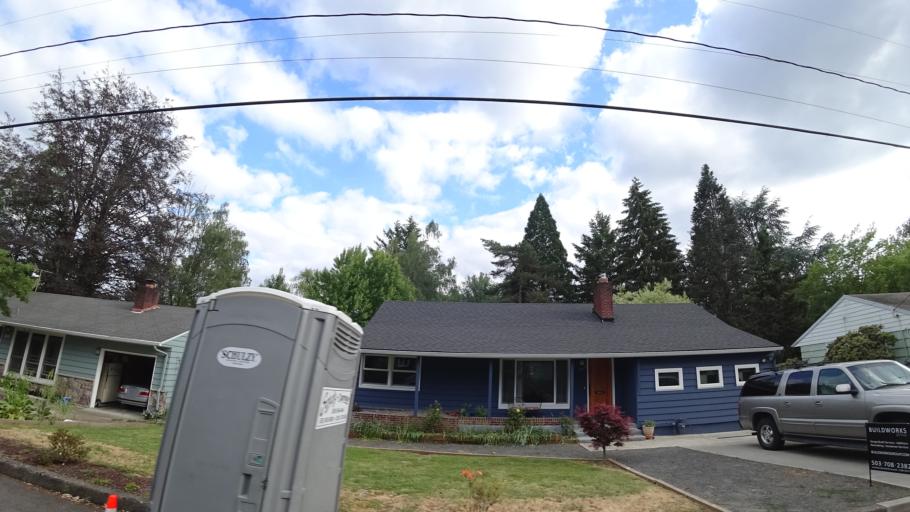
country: US
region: Oregon
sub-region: Washington County
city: Garden Home-Whitford
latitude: 45.4771
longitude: -122.7347
